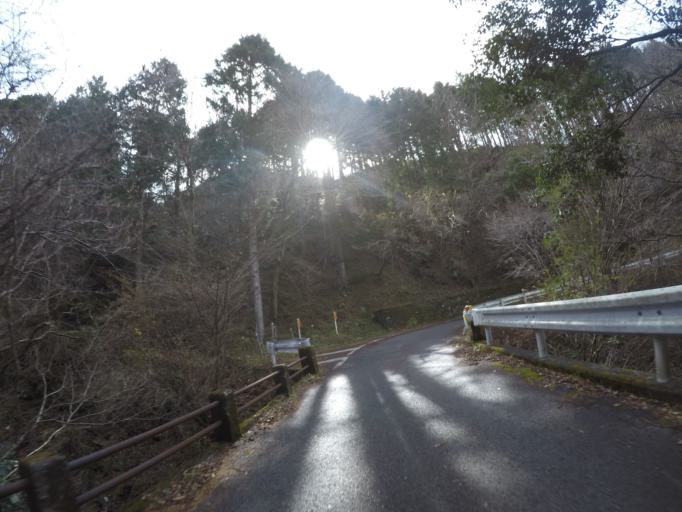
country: JP
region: Shizuoka
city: Heda
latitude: 34.8435
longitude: 138.8556
